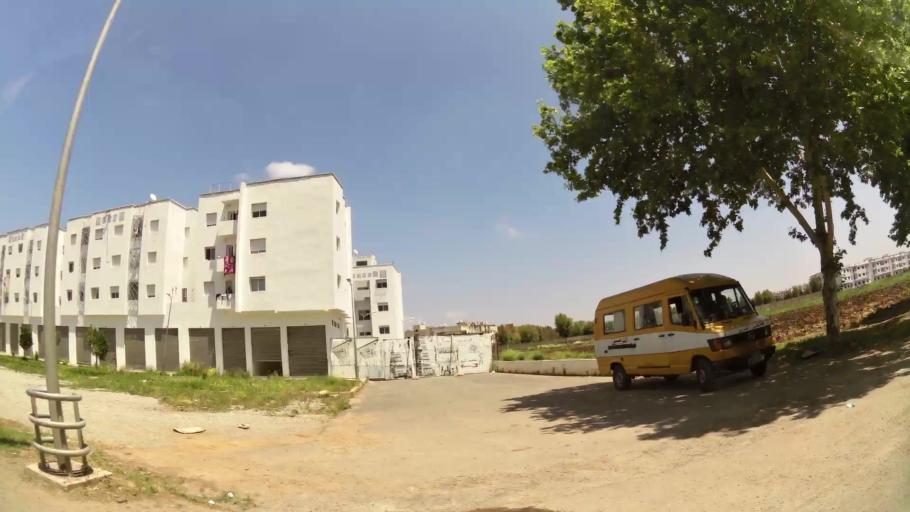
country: MA
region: Fes-Boulemane
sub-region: Fes
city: Fes
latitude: 34.0379
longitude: -5.0333
